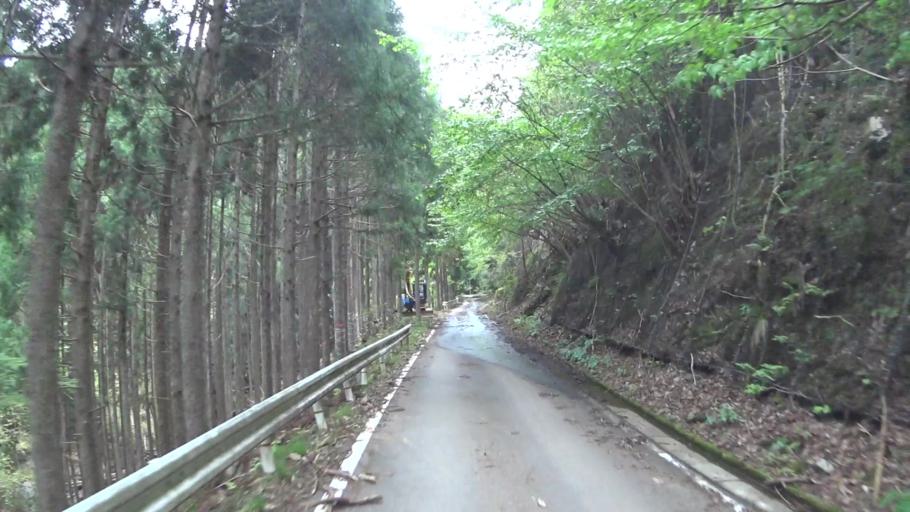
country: JP
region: Kyoto
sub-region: Kyoto-shi
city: Kamigyo-ku
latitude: 35.1783
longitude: 135.7052
